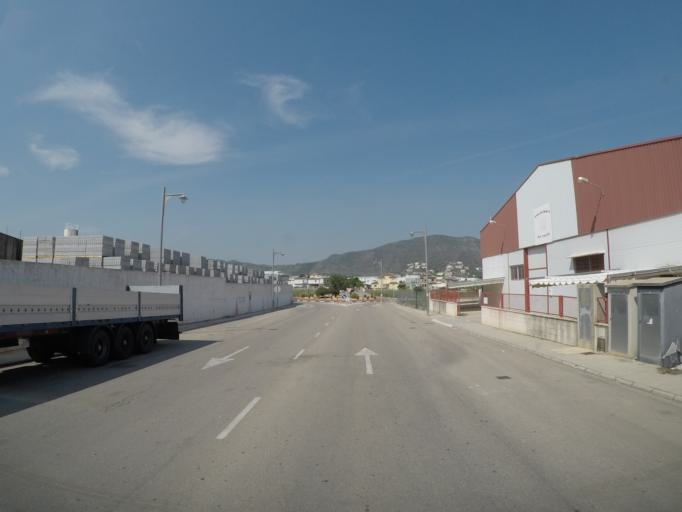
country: ES
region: Valencia
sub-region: Provincia de Alicante
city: Pego
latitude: 38.8444
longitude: -0.1085
